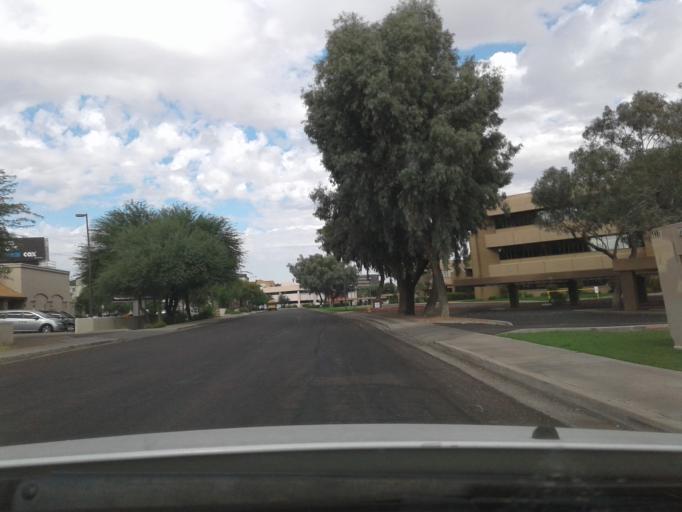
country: US
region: Arizona
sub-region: Maricopa County
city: Glendale
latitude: 33.5774
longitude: -112.1157
